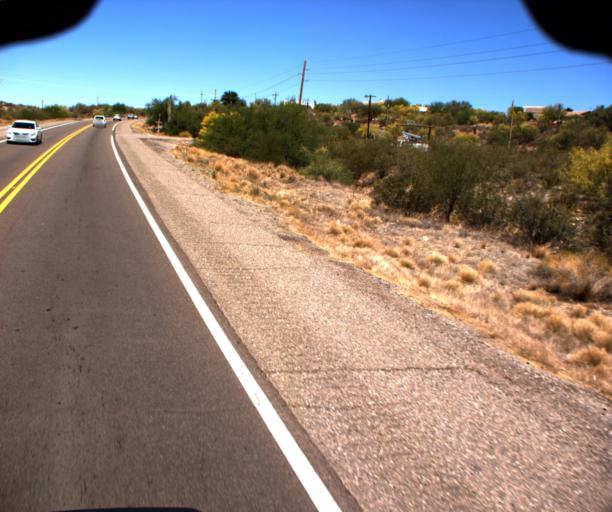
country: US
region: Arizona
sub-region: Maricopa County
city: Wickenburg
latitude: 33.9926
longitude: -112.7511
